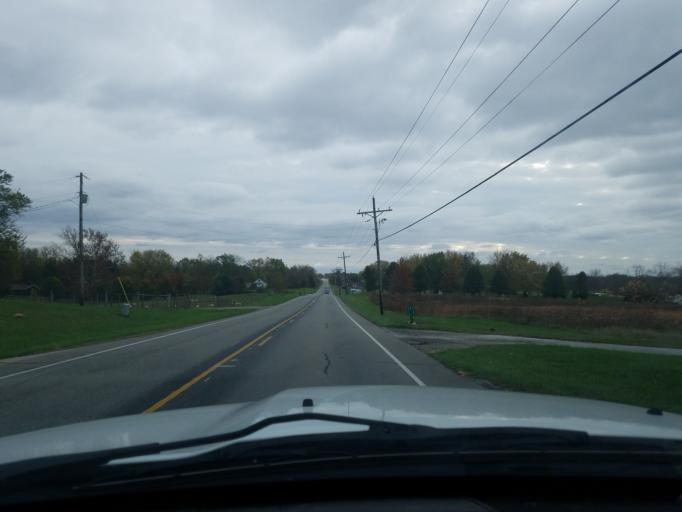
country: US
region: Indiana
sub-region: Bartholomew County
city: Hope
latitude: 39.2397
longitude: -85.7718
